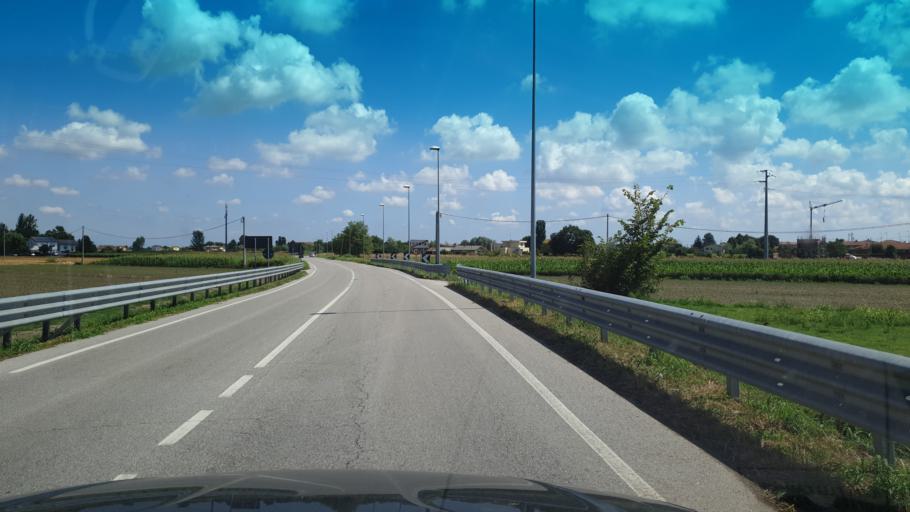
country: IT
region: Veneto
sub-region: Provincia di Rovigo
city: Costa di Rovigo
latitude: 45.0501
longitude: 11.6890
